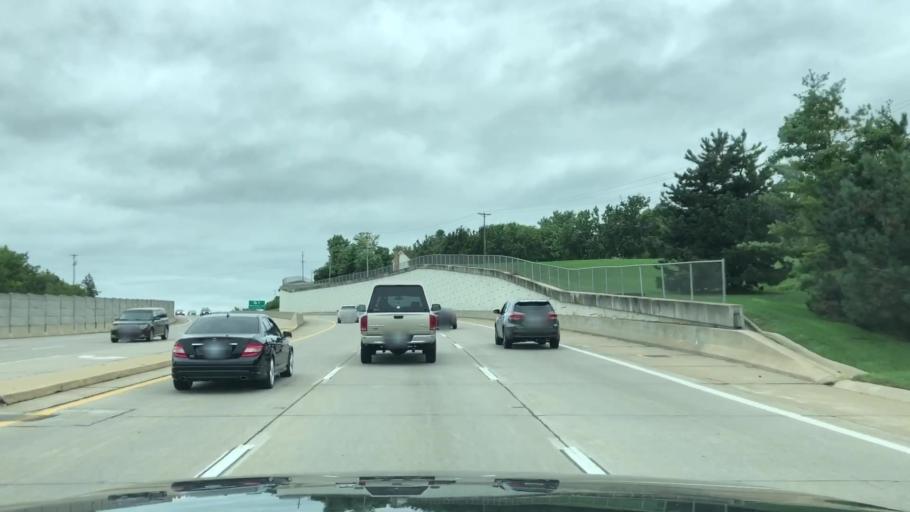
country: US
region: Missouri
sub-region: Saint Louis County
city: Manchester
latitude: 38.6044
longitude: -90.5105
